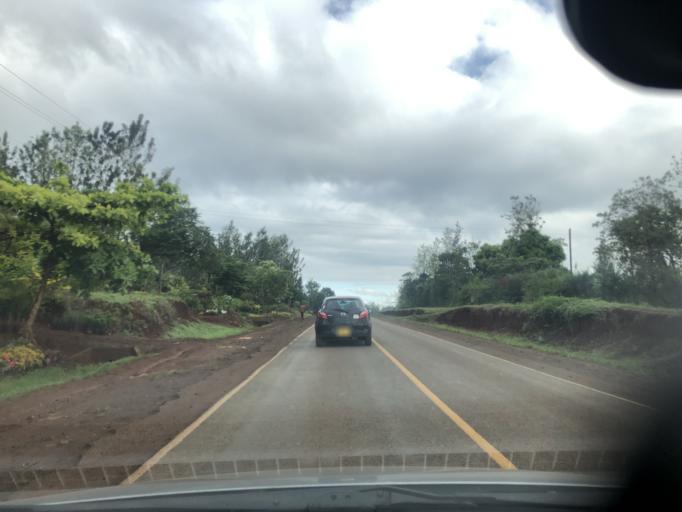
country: KE
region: Murang'a District
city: Maragua
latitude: -0.8345
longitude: 37.1376
